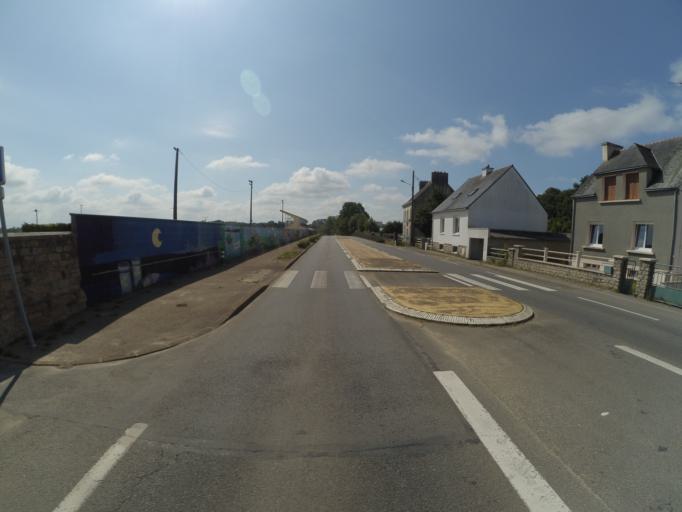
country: FR
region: Brittany
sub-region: Departement du Finistere
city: Bannalec
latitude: 47.9289
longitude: -3.6887
